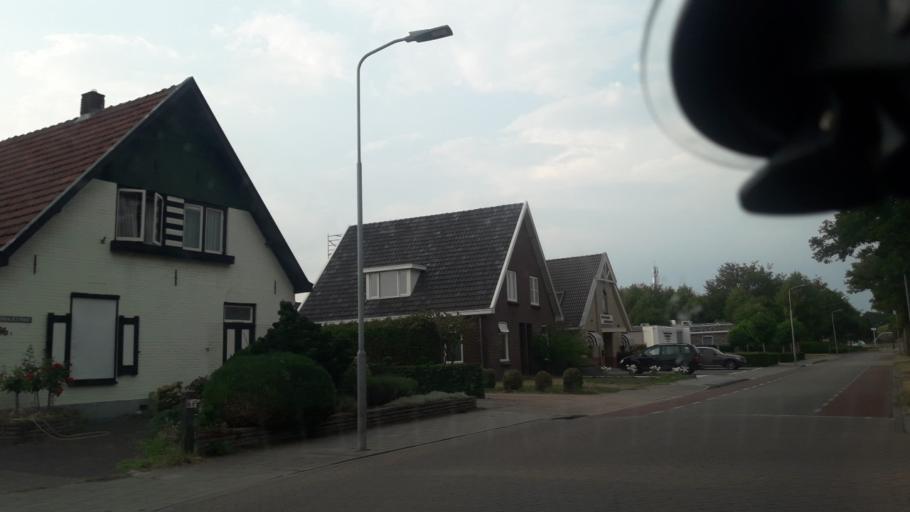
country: NL
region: Gelderland
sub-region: Oude IJsselstreek
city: Varsseveld
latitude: 51.9417
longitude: 6.4544
